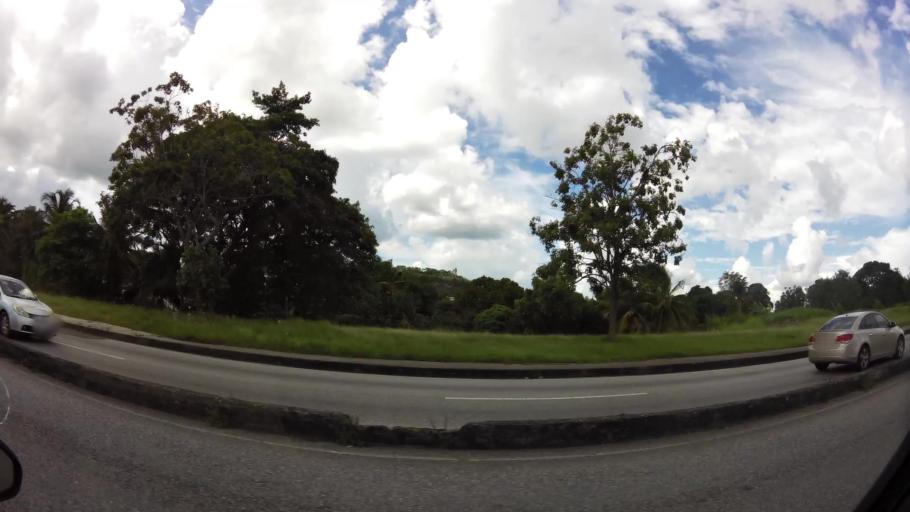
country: TT
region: City of San Fernando
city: Mon Repos
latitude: 10.2768
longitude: -61.4491
